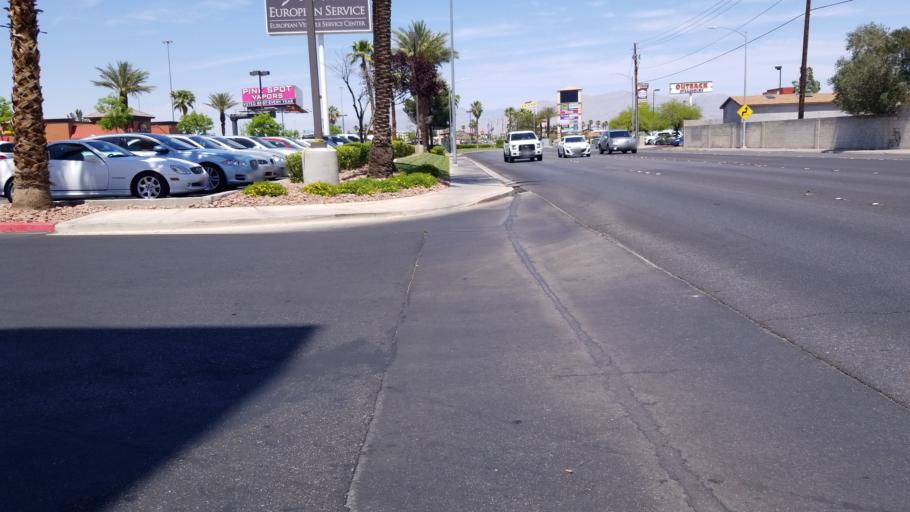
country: US
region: Nevada
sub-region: Clark County
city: Spring Valley
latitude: 36.1935
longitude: -115.2425
